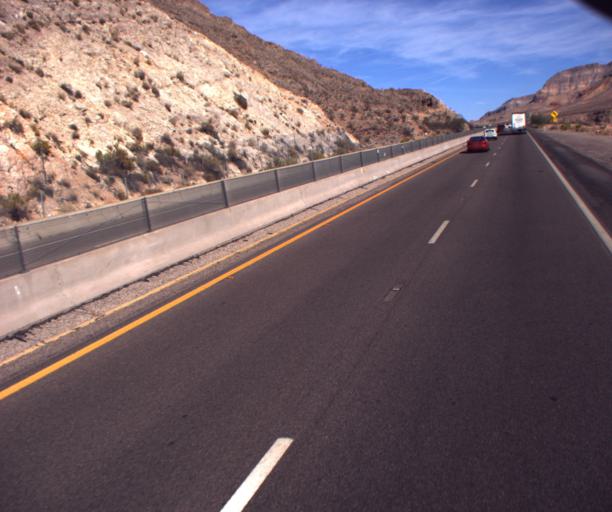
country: US
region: Arizona
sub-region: Mohave County
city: Beaver Dam
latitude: 36.9405
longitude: -113.8203
